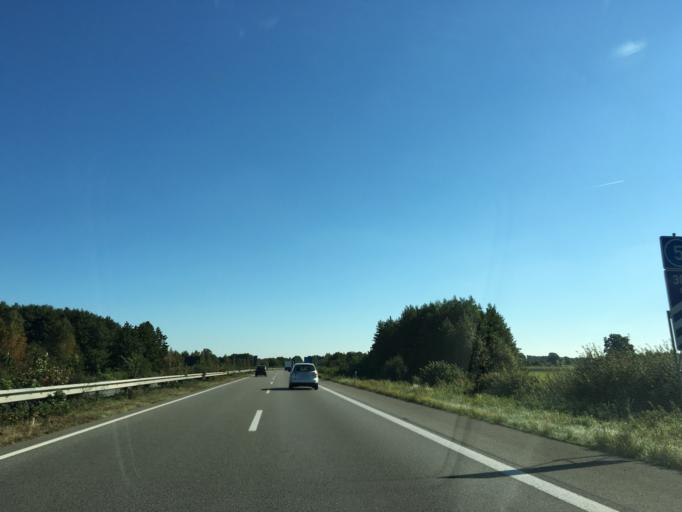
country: DE
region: Lower Saxony
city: Mechtersen
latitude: 53.3129
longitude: 10.3220
